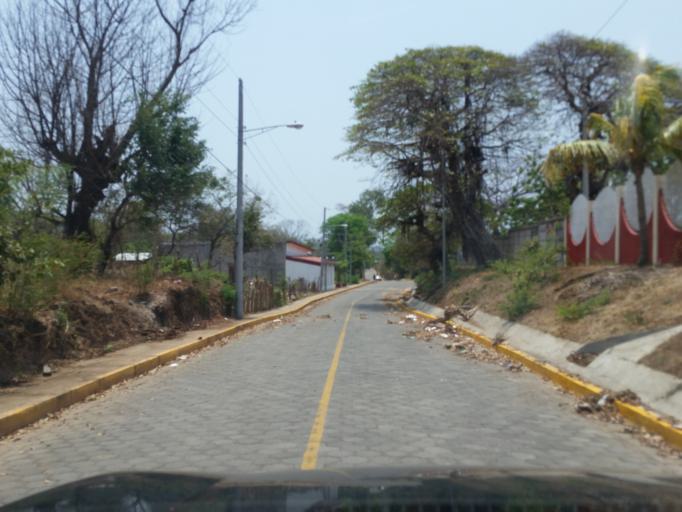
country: NI
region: Granada
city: Granada
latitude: 11.9345
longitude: -85.9736
